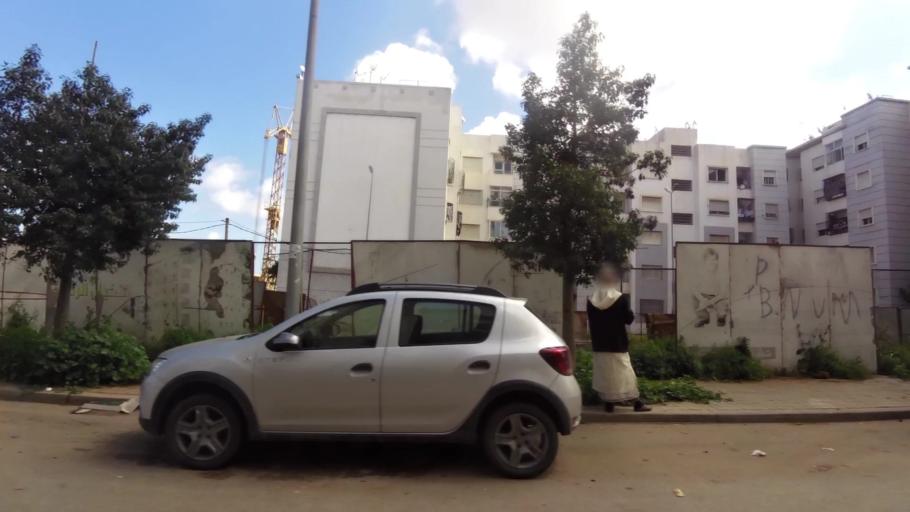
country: MA
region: Grand Casablanca
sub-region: Nouaceur
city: Dar Bouazza
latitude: 33.5352
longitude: -7.7214
